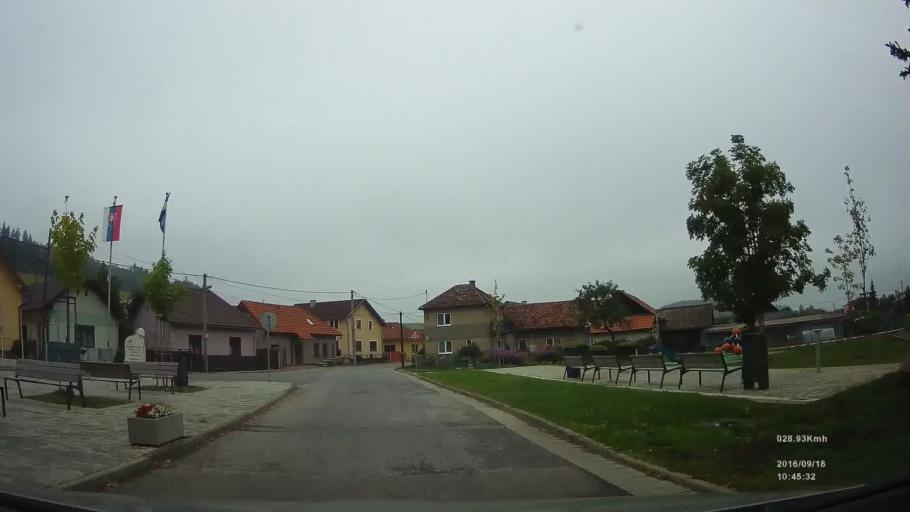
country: SK
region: Kosicky
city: Spisska Nova Ves
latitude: 48.9622
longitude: 20.5812
